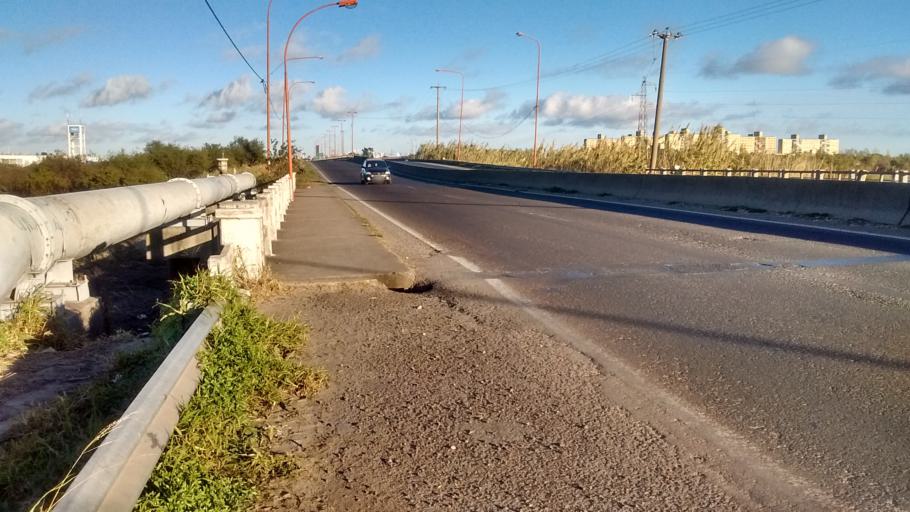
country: AR
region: Santa Fe
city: Santa Fe de la Vera Cruz
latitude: -31.6398
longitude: -60.6502
